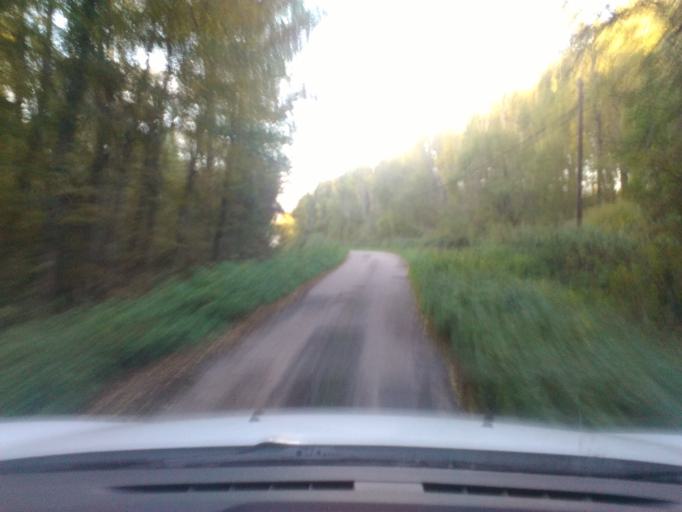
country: FR
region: Lorraine
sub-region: Departement des Vosges
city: Charmes
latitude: 48.3368
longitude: 6.2565
